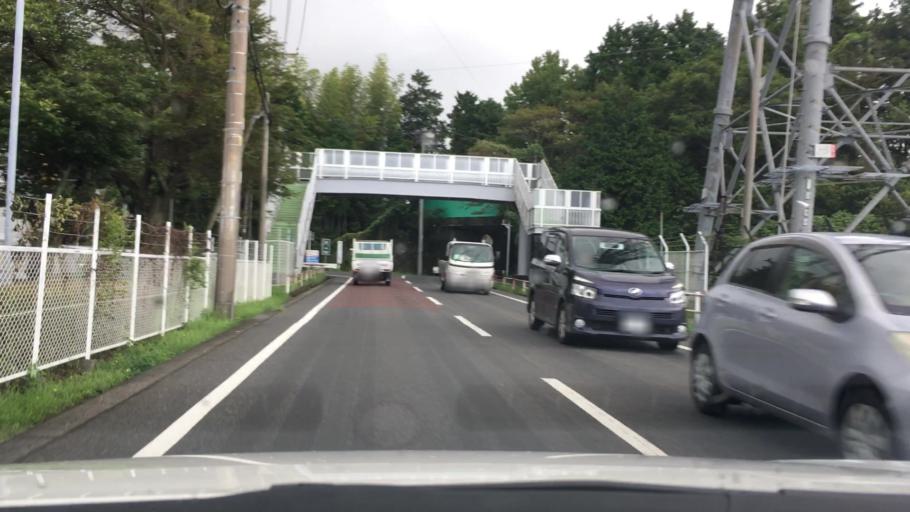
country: JP
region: Shizuoka
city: Gotemba
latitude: 35.2284
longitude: 138.8919
